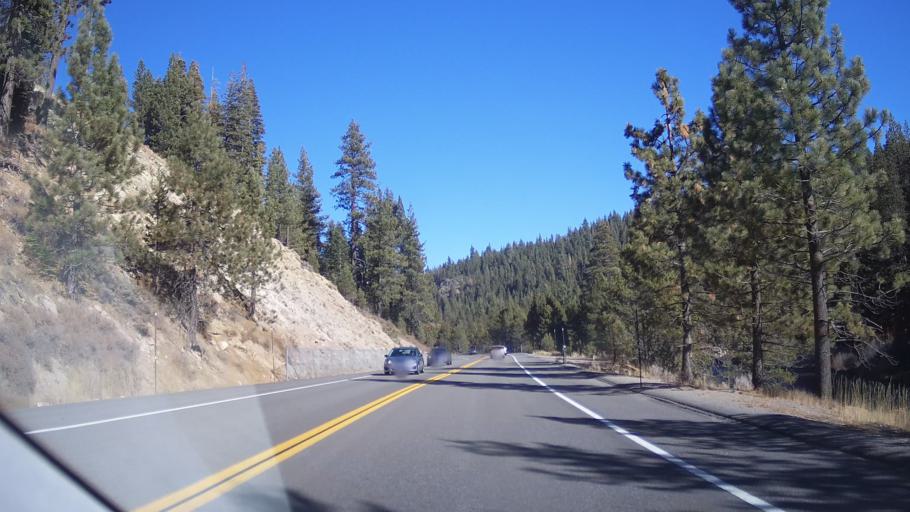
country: US
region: California
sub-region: Nevada County
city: Truckee
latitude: 39.2669
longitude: -120.2096
